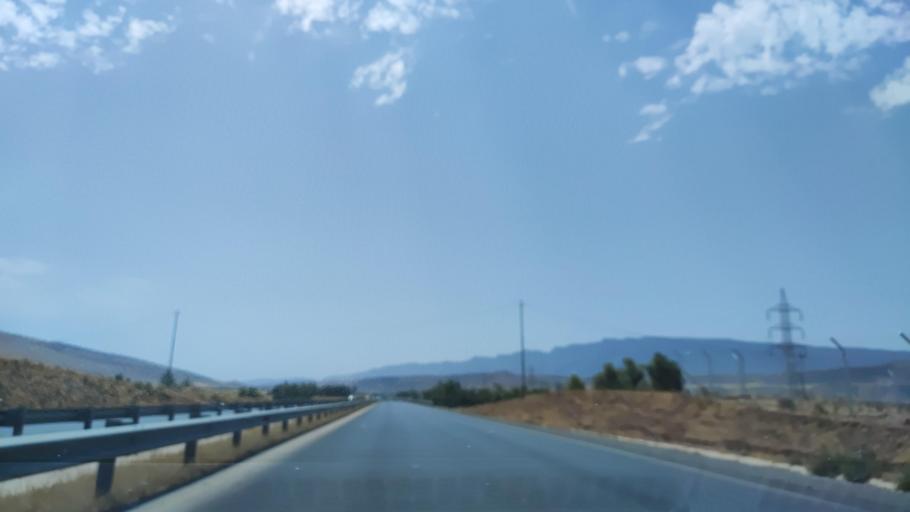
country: IQ
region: Arbil
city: Shaqlawah
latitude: 36.4763
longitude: 44.3806
